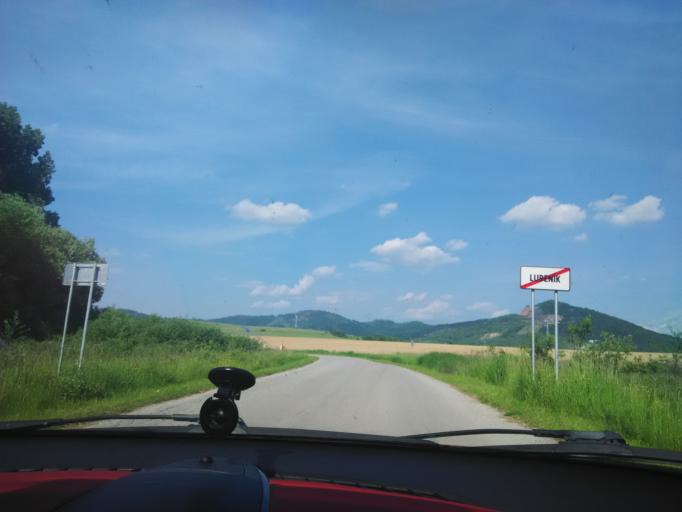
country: SK
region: Banskobystricky
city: Revuca
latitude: 48.6573
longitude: 20.1994
